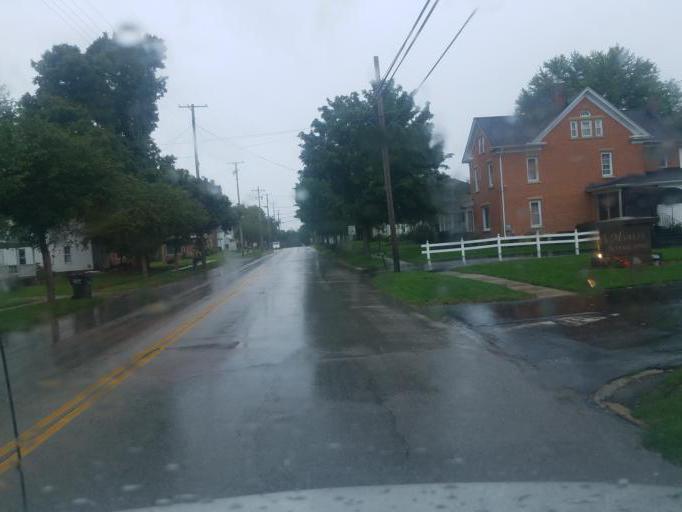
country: US
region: Ohio
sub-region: Wayne County
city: Creston
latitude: 40.9798
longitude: -81.8983
